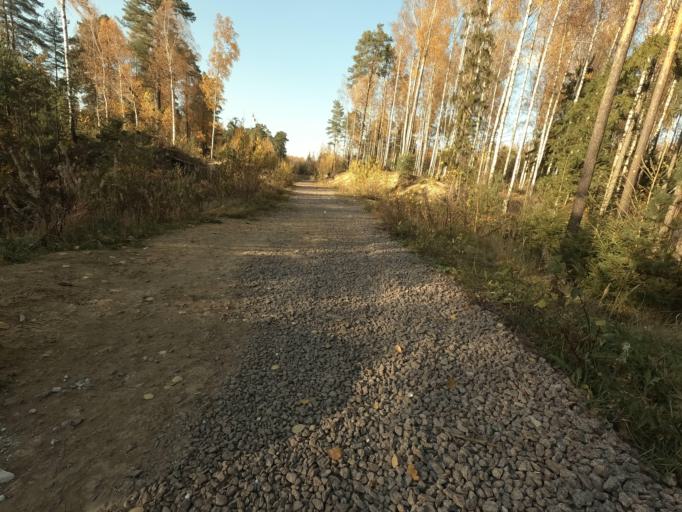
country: RU
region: Leningrad
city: Sertolovo
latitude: 60.1500
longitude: 30.2225
